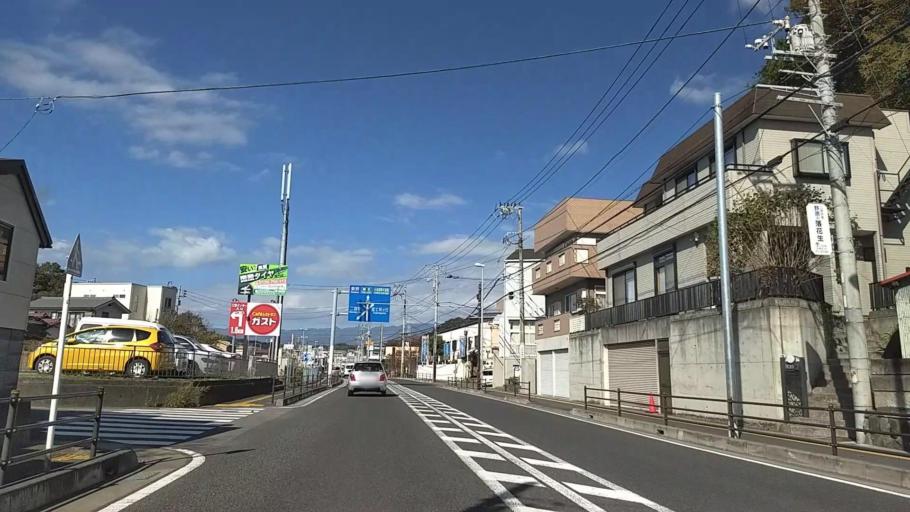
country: JP
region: Kanagawa
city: Ninomiya
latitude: 35.3024
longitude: 139.2580
